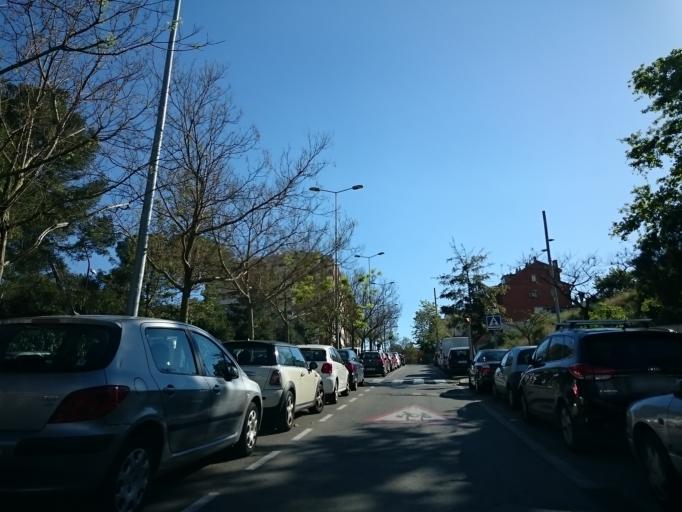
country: ES
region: Catalonia
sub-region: Provincia de Barcelona
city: Viladecans
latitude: 41.3239
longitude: 2.0115
